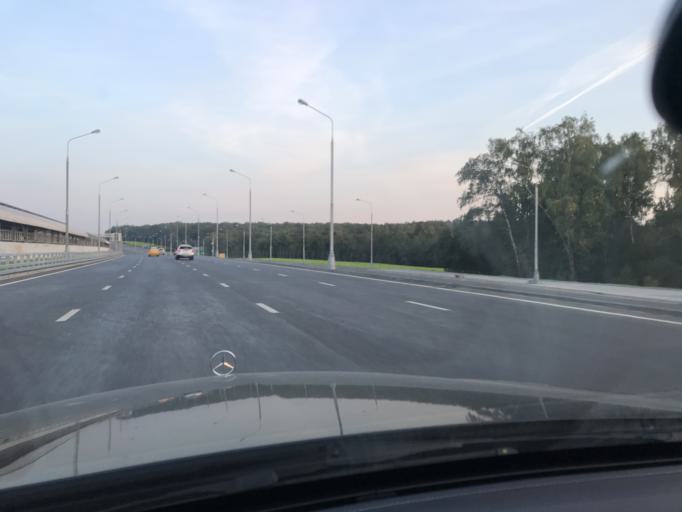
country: RU
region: Moskovskaya
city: Mosrentgen
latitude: 55.5908
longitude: 37.4231
